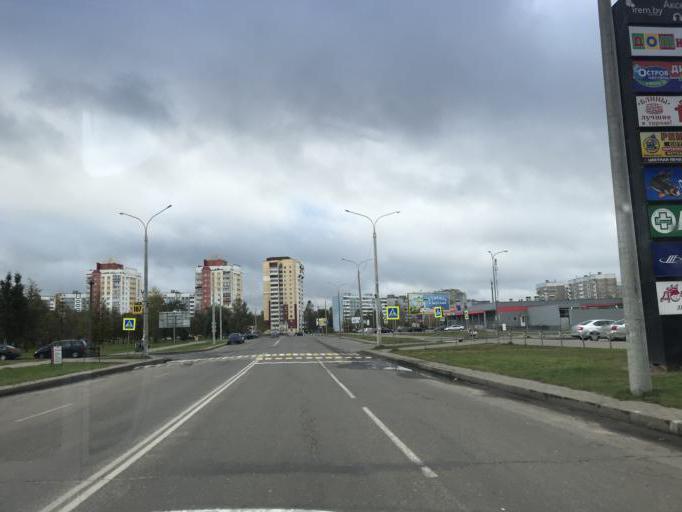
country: BY
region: Mogilev
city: Mahilyow
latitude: 53.8818
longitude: 30.3684
